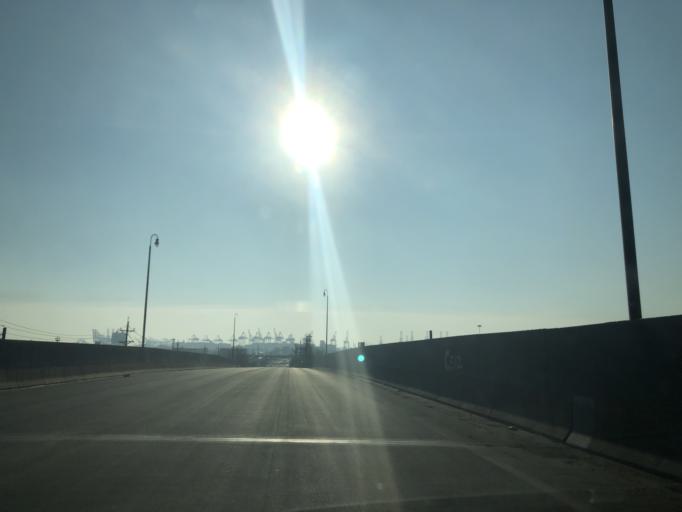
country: US
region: New Jersey
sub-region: Hudson County
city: Bayonne
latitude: 40.7063
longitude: -74.1344
